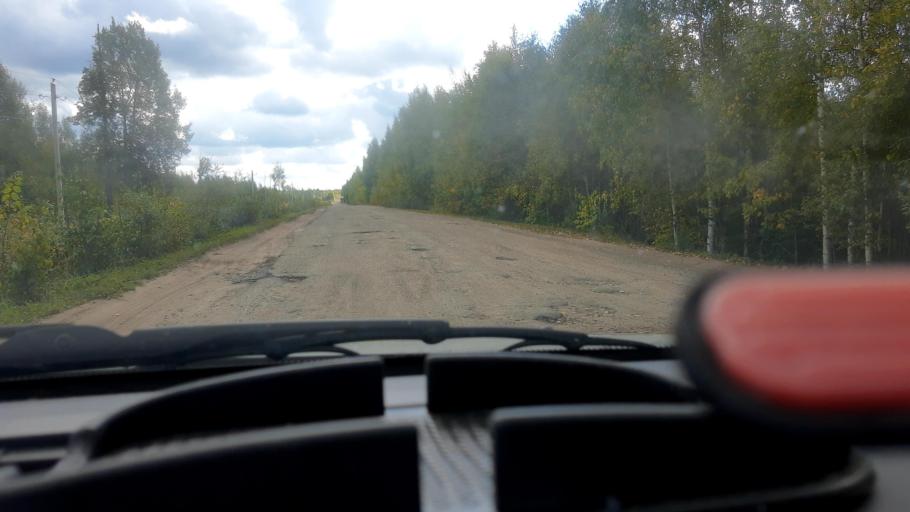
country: RU
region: Mariy-El
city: Kilemary
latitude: 56.8906
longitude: 46.7563
